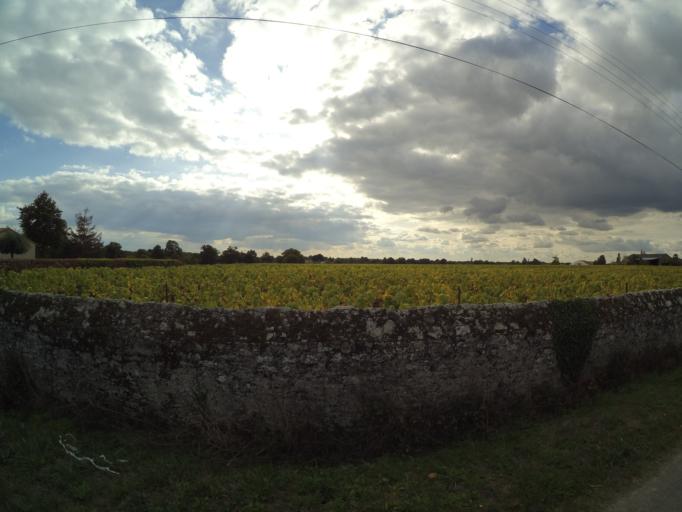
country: FR
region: Pays de la Loire
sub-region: Departement de la Loire-Atlantique
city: Maisdon-sur-Sevre
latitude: 47.0785
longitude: -1.3720
